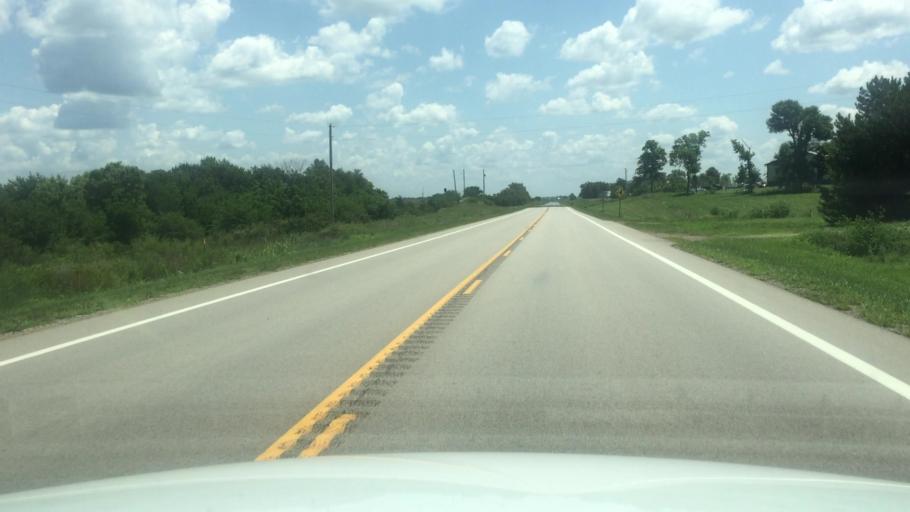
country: US
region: Kansas
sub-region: Brown County
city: Horton
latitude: 39.6073
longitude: -95.3422
